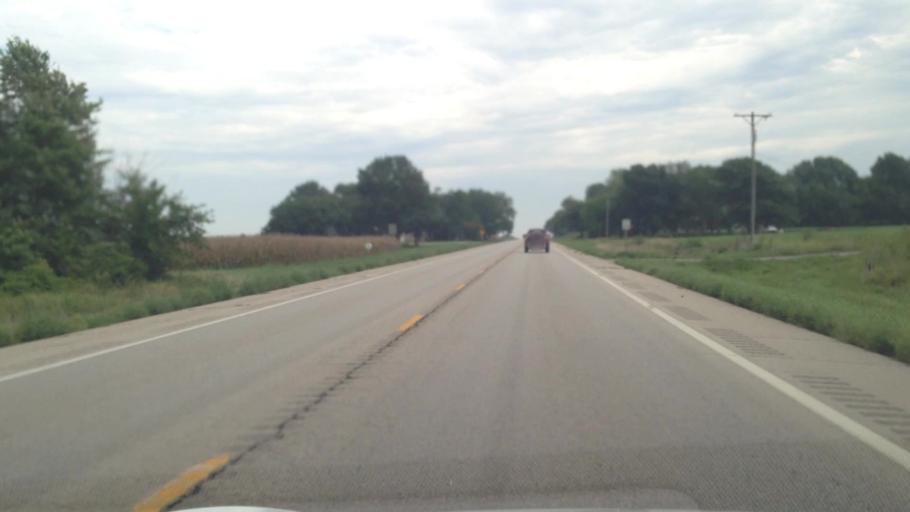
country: US
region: Kansas
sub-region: Crawford County
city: Pittsburg
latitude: 37.3393
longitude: -94.8103
